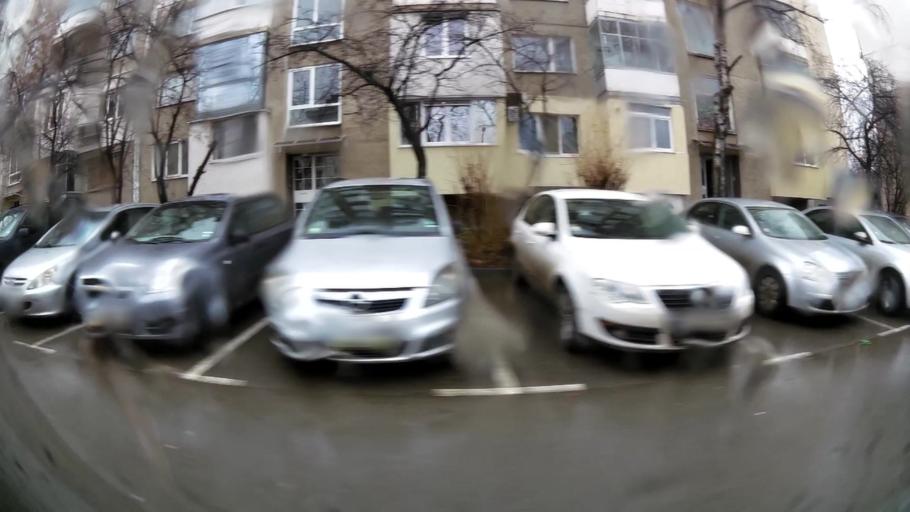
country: BG
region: Sofia-Capital
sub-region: Stolichna Obshtina
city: Sofia
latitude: 42.6546
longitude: 23.3756
